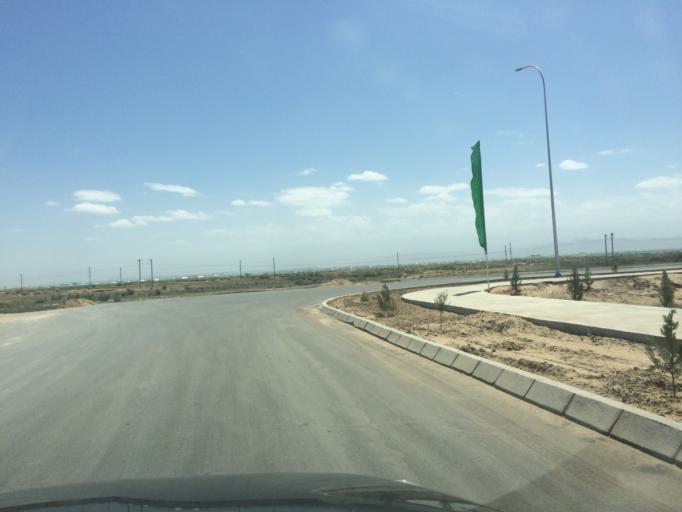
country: TM
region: Ahal
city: Abadan
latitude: 38.0935
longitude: 58.2940
